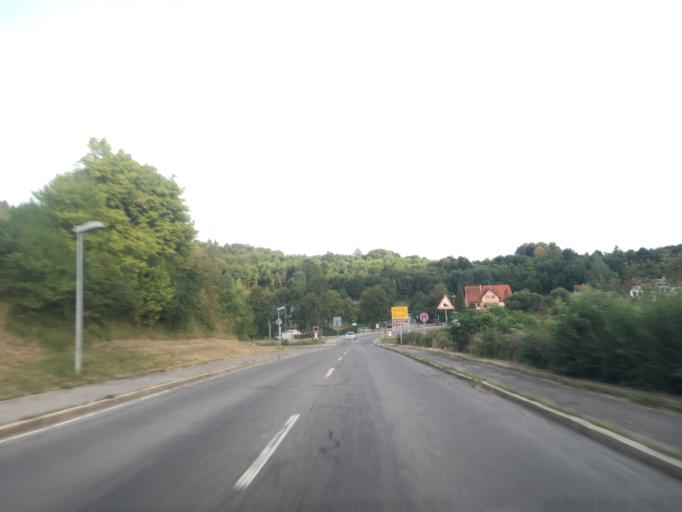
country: DE
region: Baden-Wuerttemberg
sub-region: Tuebingen Region
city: Gomadingen
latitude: 48.3836
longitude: 9.4200
